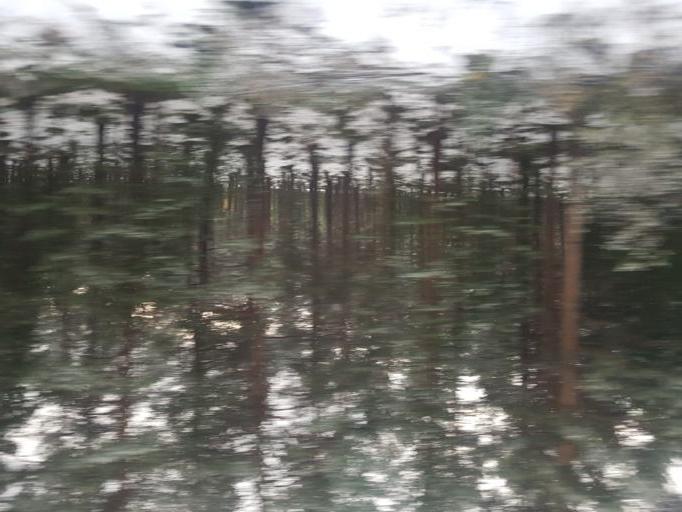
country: NO
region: Oppland
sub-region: Dovre
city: Dombas
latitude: 62.0764
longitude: 9.1286
